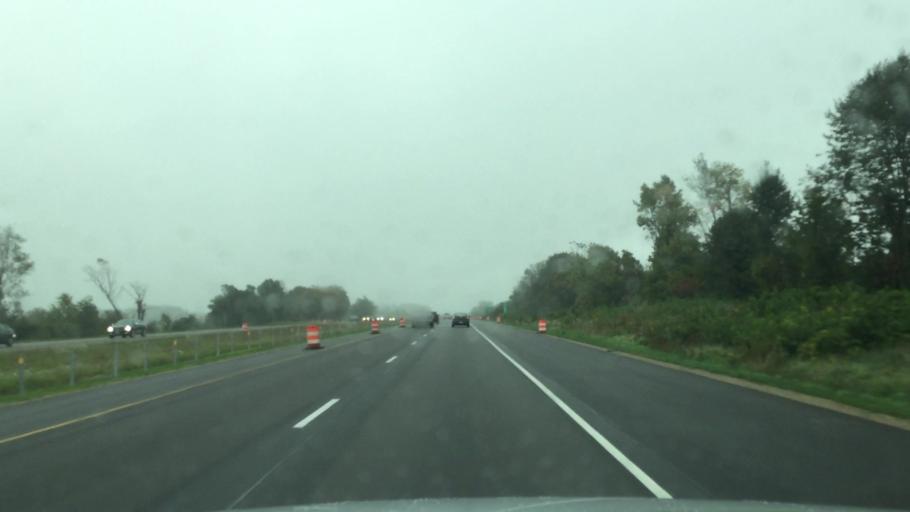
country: US
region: Michigan
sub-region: Van Buren County
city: Hartford
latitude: 42.1971
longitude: -86.0832
